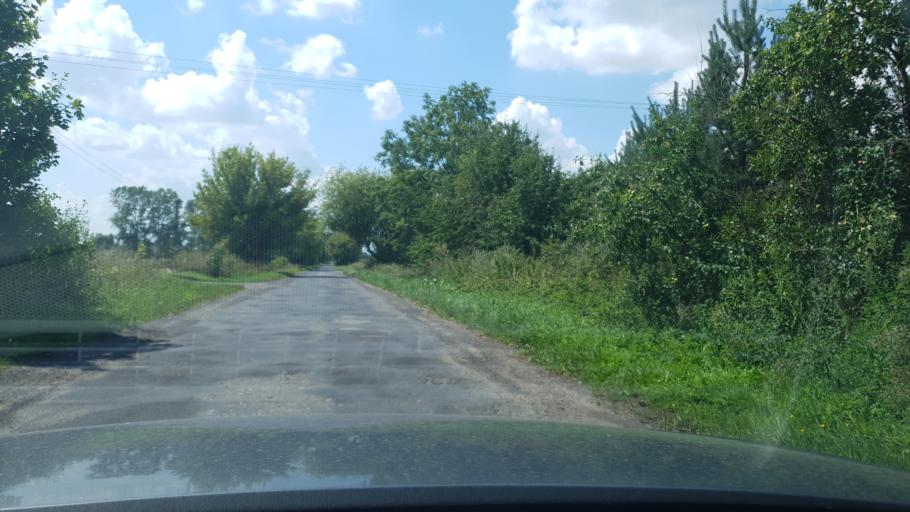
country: PL
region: Kujawsko-Pomorskie
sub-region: Powiat wabrzeski
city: Pluznica
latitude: 53.3098
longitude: 18.8188
